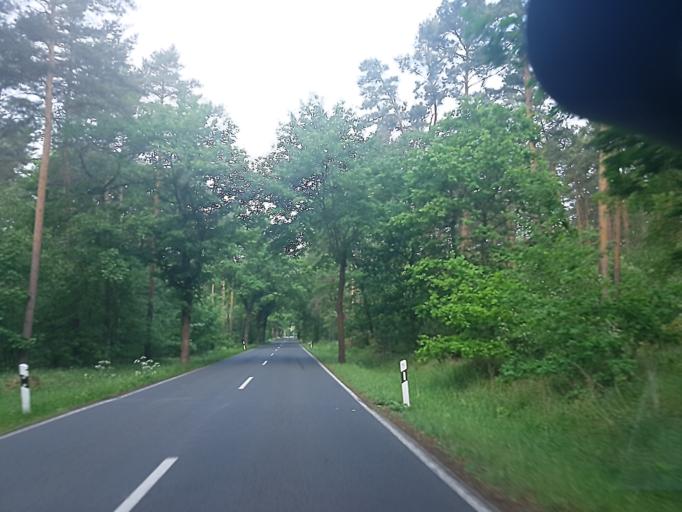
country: DE
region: Saxony-Anhalt
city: Rosslau
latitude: 51.9904
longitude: 12.2880
